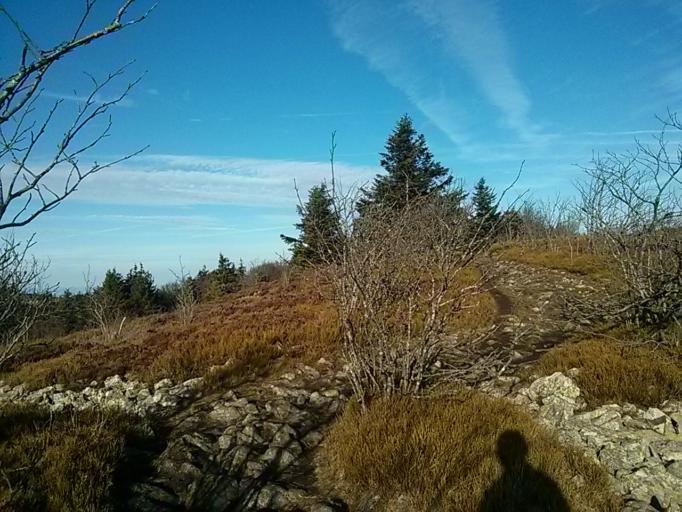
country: FR
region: Rhone-Alpes
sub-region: Departement de la Loire
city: Saint-Julien-Molin-Molette
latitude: 45.3800
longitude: 4.5812
